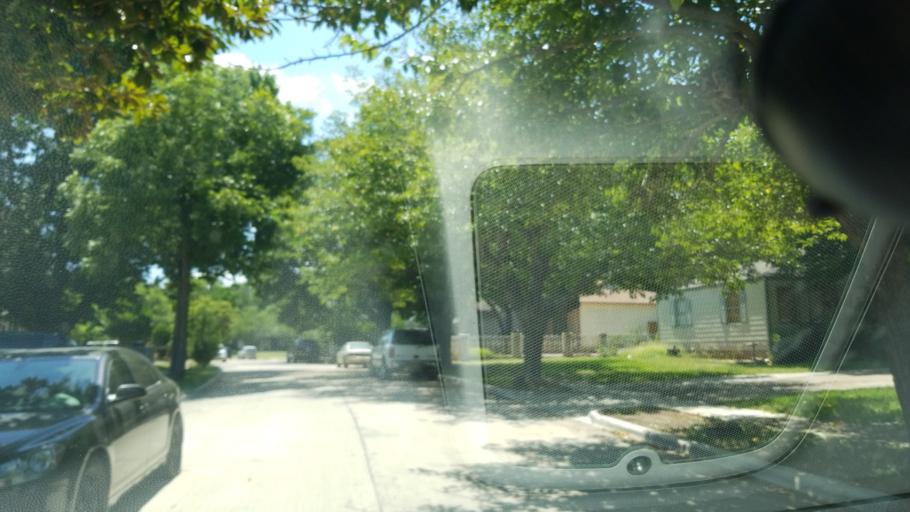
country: US
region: Texas
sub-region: Dallas County
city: Cockrell Hill
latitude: 32.7159
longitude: -96.8412
